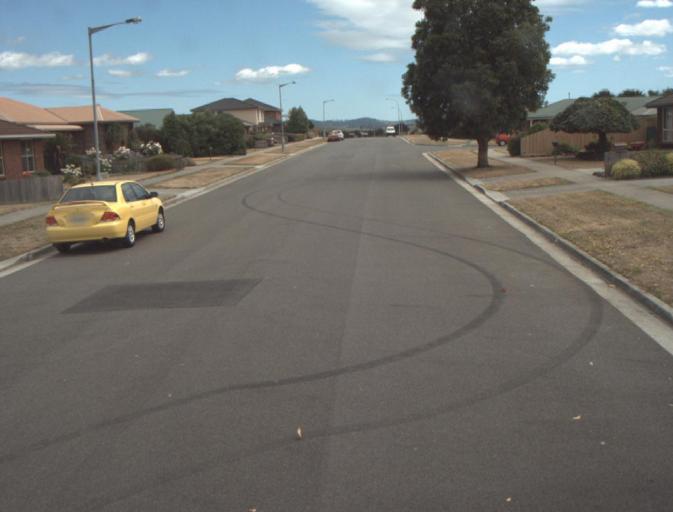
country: AU
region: Tasmania
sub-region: Launceston
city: Invermay
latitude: -41.3910
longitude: 147.1150
